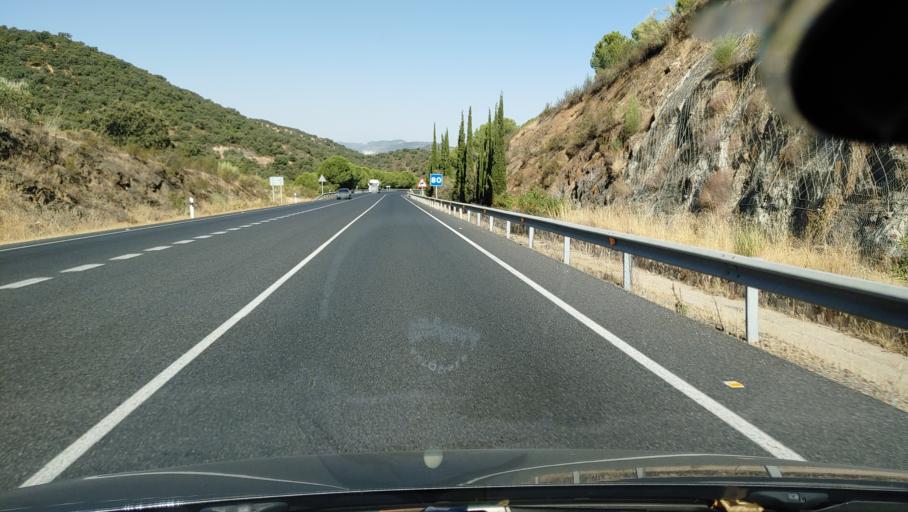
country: ES
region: Andalusia
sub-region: Province of Cordoba
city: Villaharta
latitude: 38.1125
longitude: -4.8842
